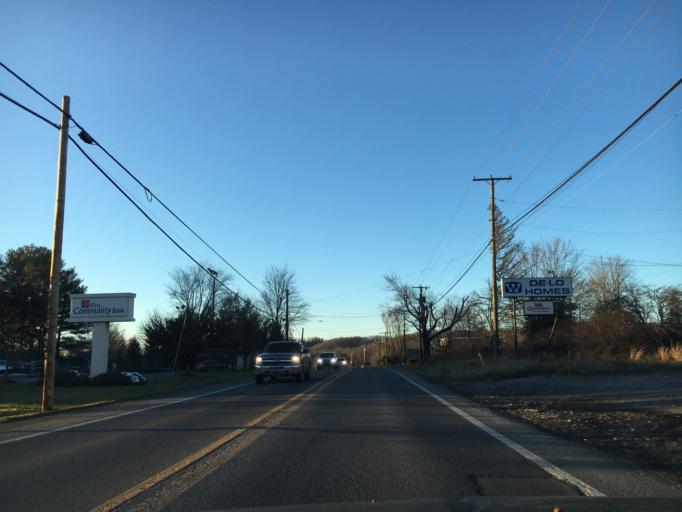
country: US
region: West Virginia
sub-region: Raleigh County
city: Daniels
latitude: 37.7440
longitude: -81.1238
